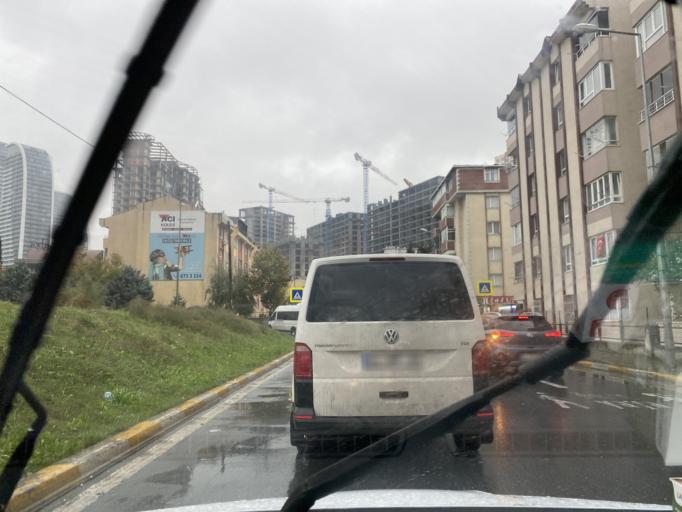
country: TR
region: Istanbul
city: Esenyurt
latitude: 41.0193
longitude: 28.6759
